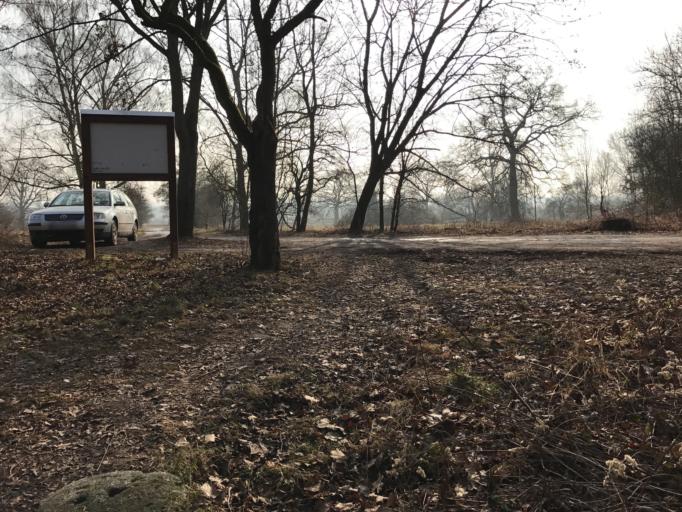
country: DE
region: Rheinland-Pfalz
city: Budenheim
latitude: 50.0236
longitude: 8.1467
